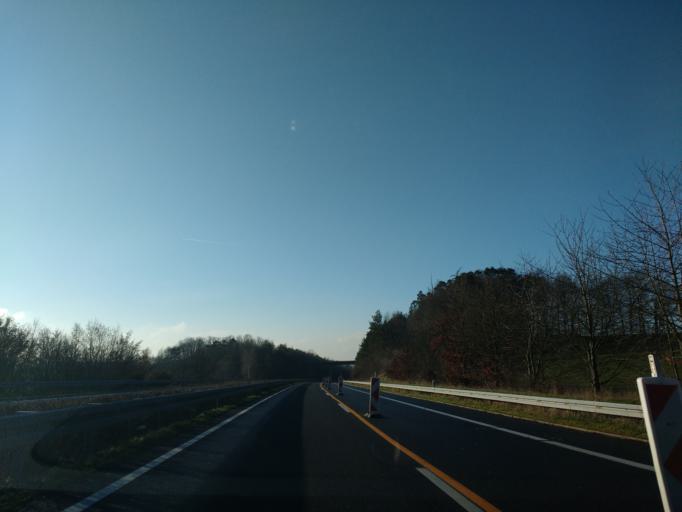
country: DE
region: Hesse
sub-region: Regierungsbezirk Kassel
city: Neuental
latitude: 51.0198
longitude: 9.2250
